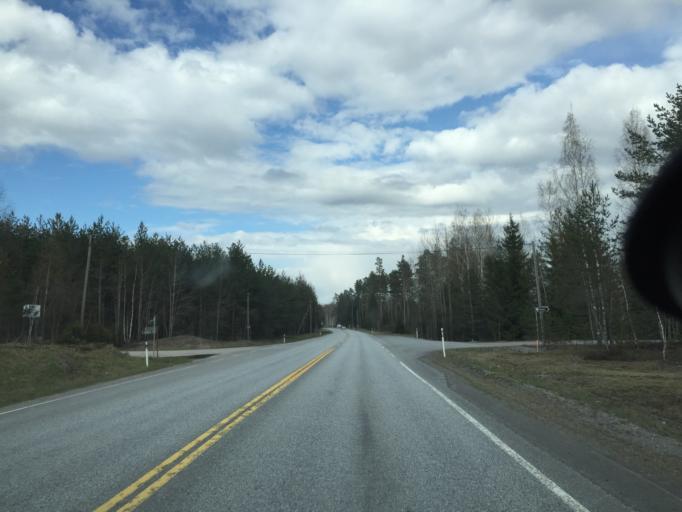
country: FI
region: Uusimaa
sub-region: Raaseporin
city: Inga
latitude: 60.1566
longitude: 23.9238
